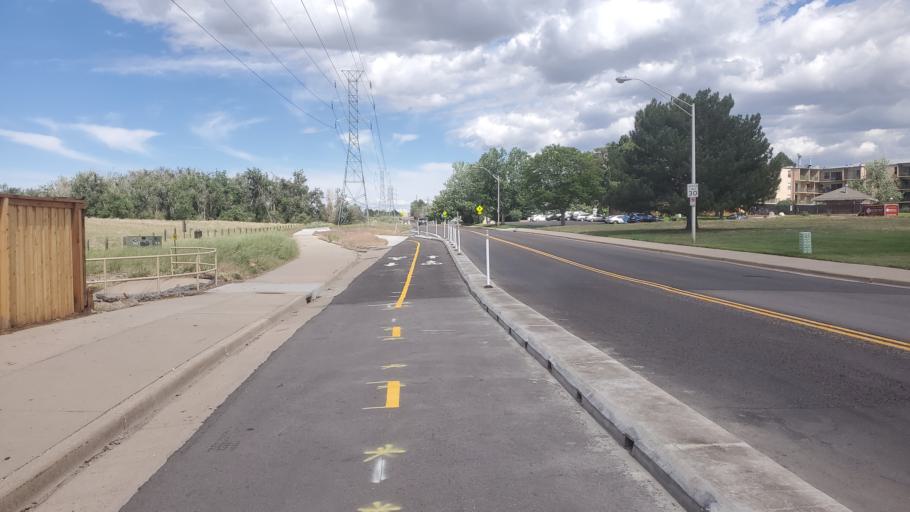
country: US
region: Colorado
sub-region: Adams County
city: Aurora
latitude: 39.6821
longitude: -104.8387
